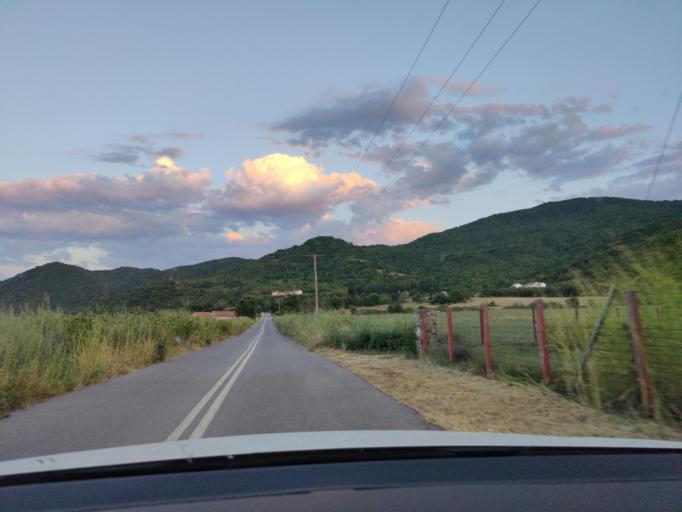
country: GR
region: Central Macedonia
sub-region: Nomos Serron
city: Chrysochorafa
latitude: 41.1791
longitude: 23.1111
